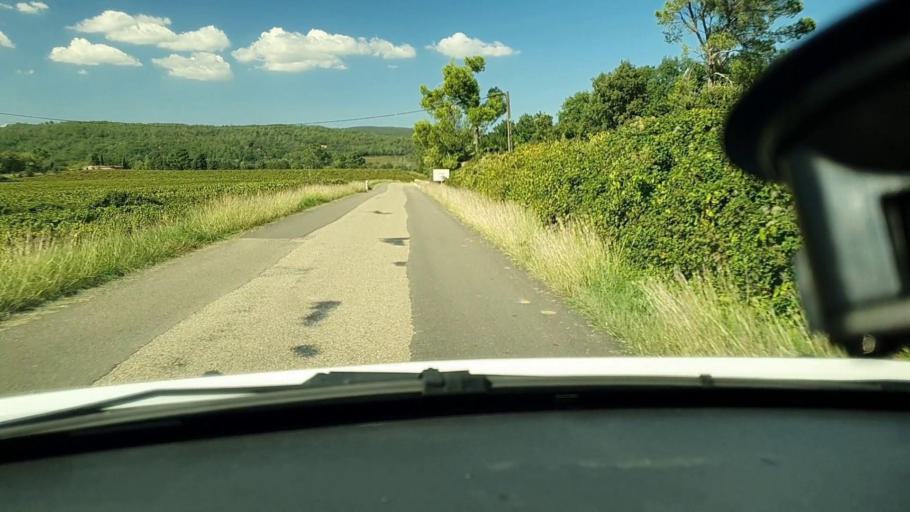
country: FR
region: Languedoc-Roussillon
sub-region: Departement du Gard
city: Goudargues
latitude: 44.1810
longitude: 4.4865
